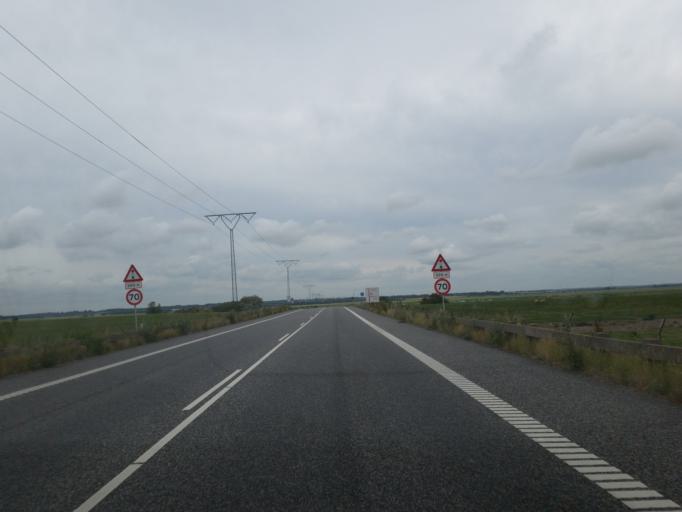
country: DK
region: South Denmark
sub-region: Tonder Kommune
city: Sherrebek
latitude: 55.1530
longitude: 8.6976
